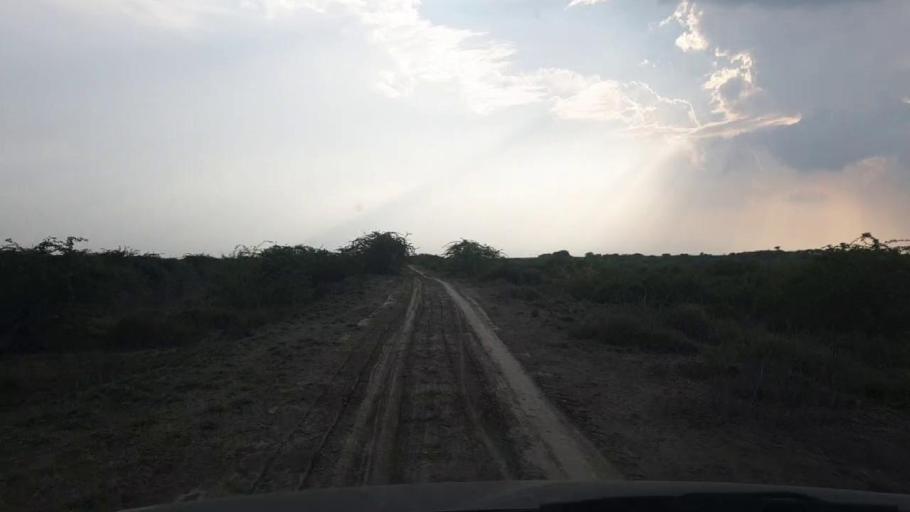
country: PK
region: Sindh
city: Badin
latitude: 24.4690
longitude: 68.6955
